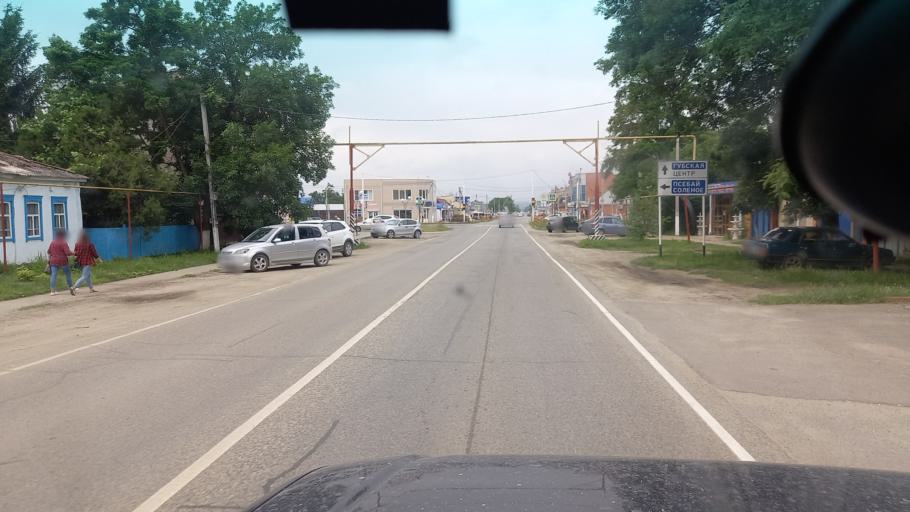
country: RU
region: Krasnodarskiy
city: Mostovskoy
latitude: 44.4088
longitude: 40.8046
